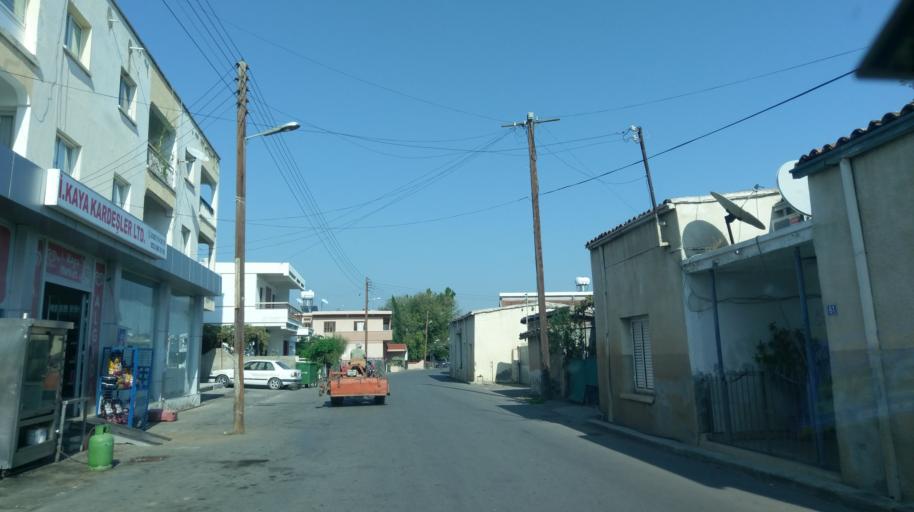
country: CY
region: Lefkosia
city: Morfou
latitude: 35.1968
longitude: 32.9860
